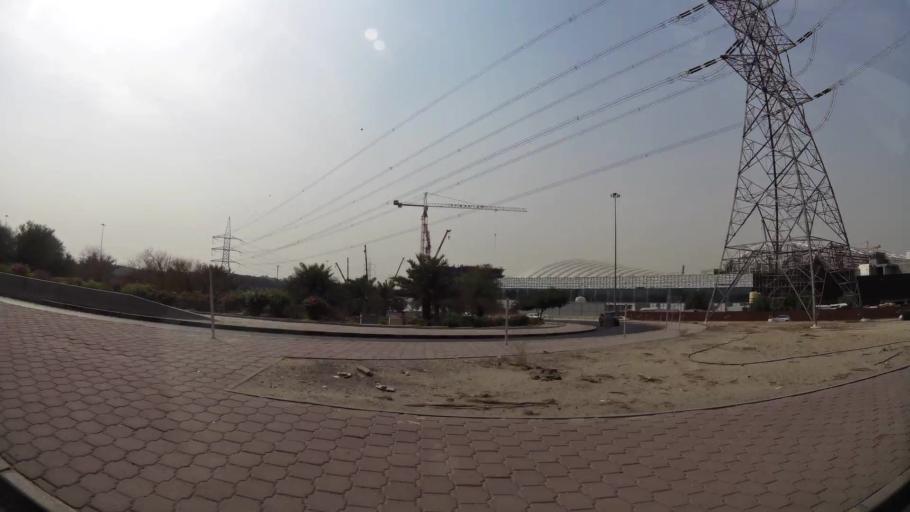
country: KW
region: Al Asimah
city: Ar Rabiyah
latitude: 29.3028
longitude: 47.9449
